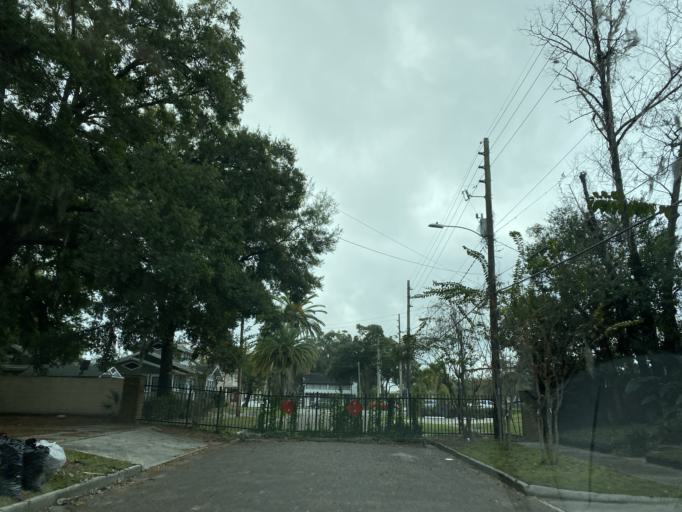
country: US
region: Florida
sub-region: Orange County
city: Orlando
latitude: 28.5537
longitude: -81.3888
